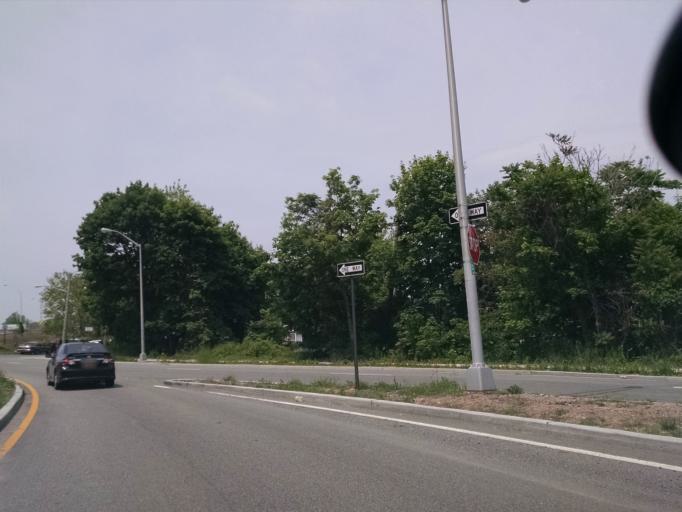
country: US
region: New York
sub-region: Kings County
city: Bensonhurst
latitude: 40.6046
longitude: -74.0663
